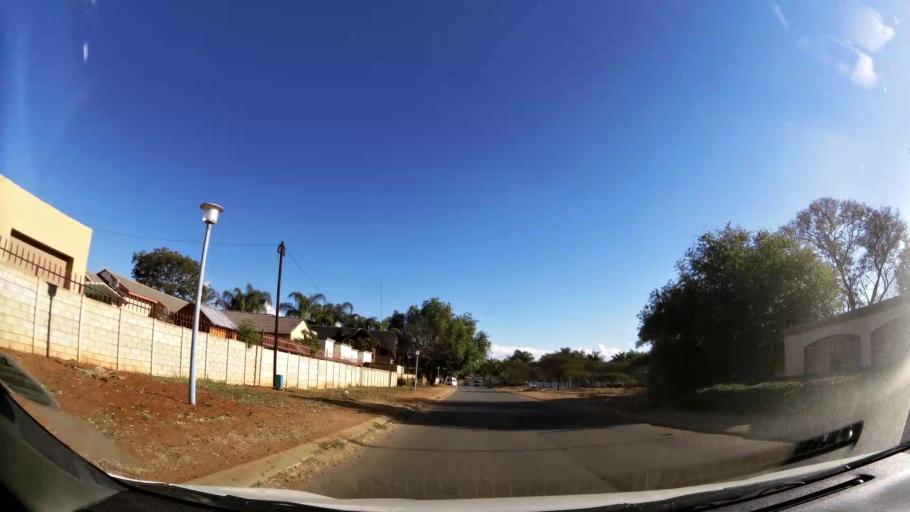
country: ZA
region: Limpopo
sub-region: Capricorn District Municipality
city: Polokwane
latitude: -23.8856
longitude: 29.4941
